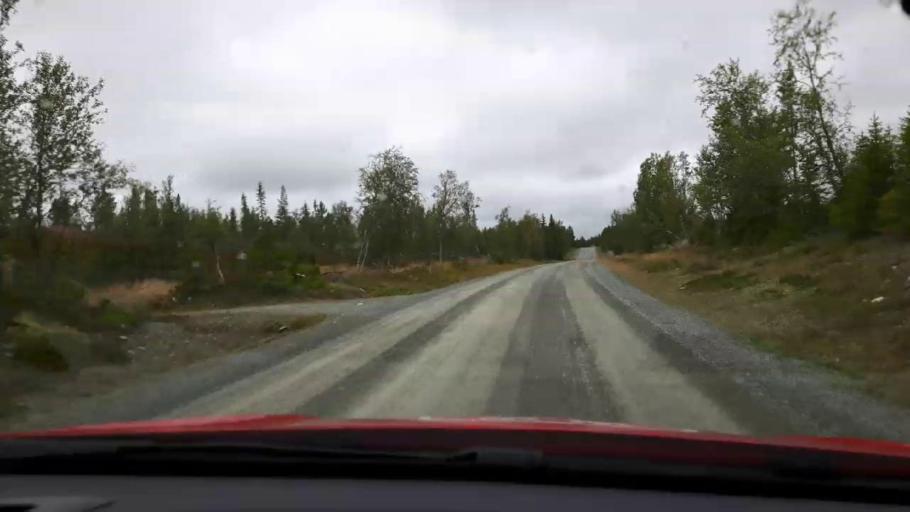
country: SE
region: Jaemtland
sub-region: Bergs Kommun
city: Hoverberg
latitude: 62.9055
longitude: 14.0724
